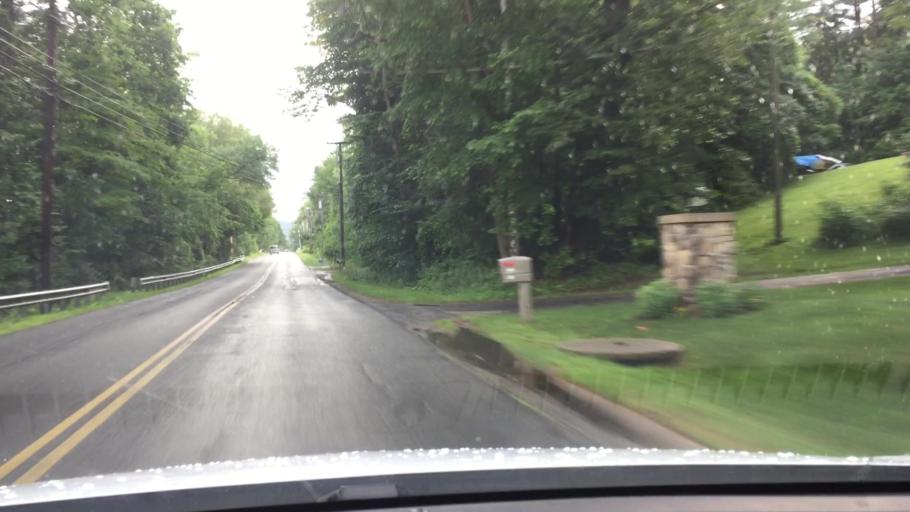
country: US
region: Massachusetts
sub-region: Berkshire County
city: Dalton
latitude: 42.4413
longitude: -73.1940
